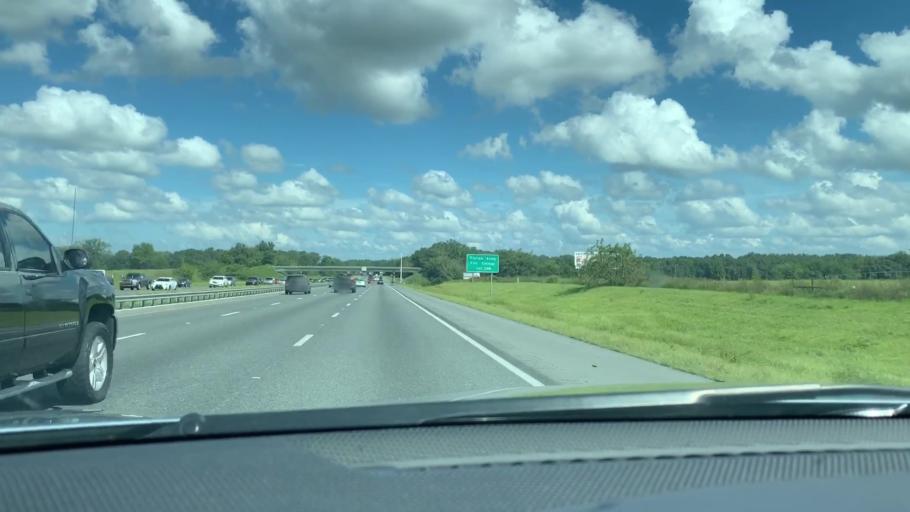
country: US
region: Florida
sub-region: Marion County
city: Ocala
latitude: 29.2491
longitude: -82.1897
